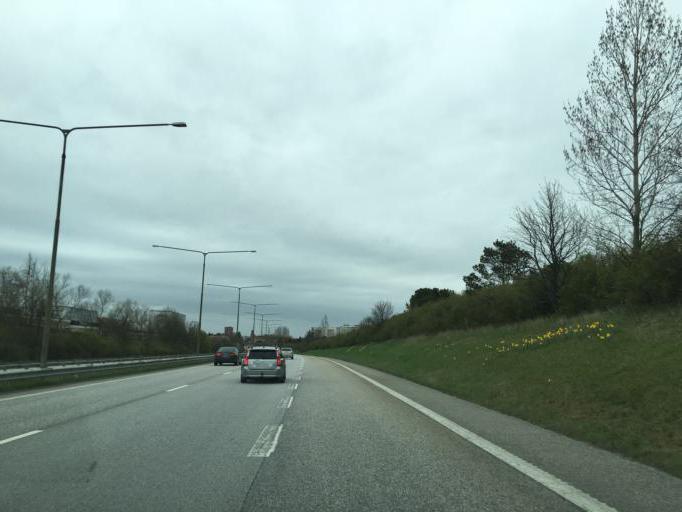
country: SE
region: Skane
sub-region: Malmo
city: Malmoe
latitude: 55.5691
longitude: 13.0039
